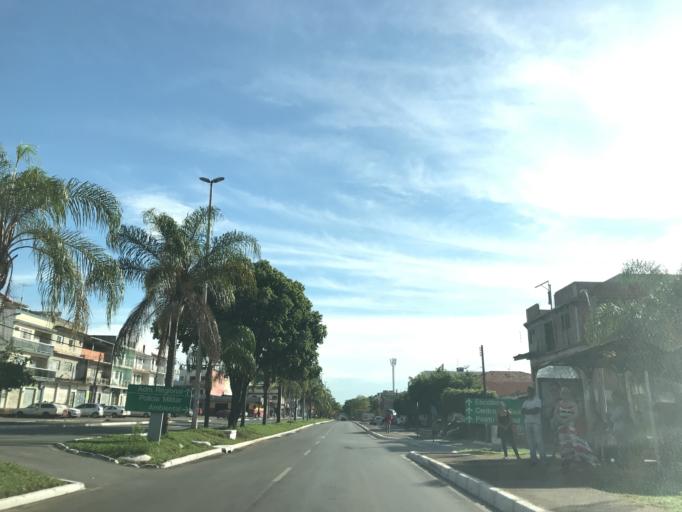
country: BR
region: Federal District
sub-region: Brasilia
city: Brasilia
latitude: -15.8575
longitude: -47.9547
